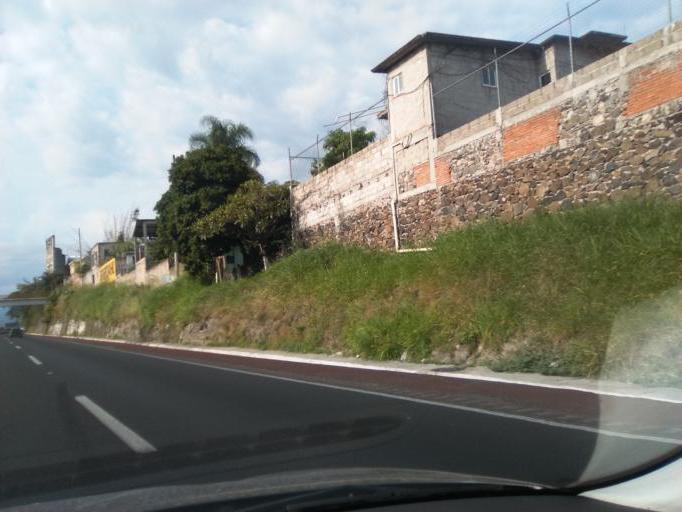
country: MX
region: Morelos
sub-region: Emiliano Zapata
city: Tres de Mayo
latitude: 18.8764
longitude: -99.2277
